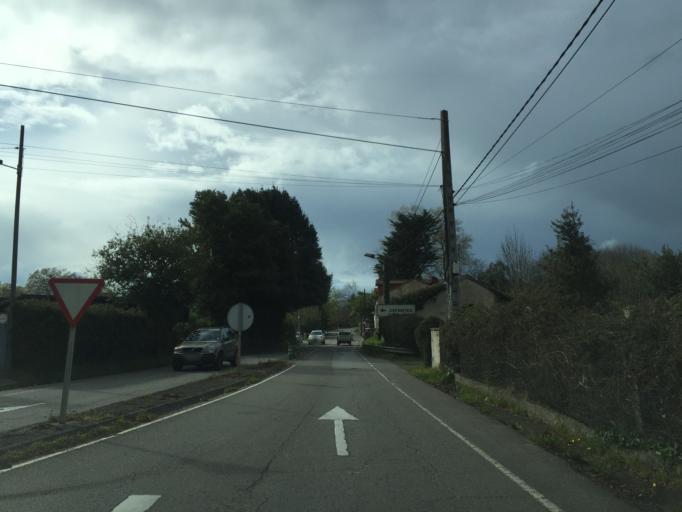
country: ES
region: Asturias
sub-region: Province of Asturias
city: Gijon
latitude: 43.5163
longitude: -5.6041
